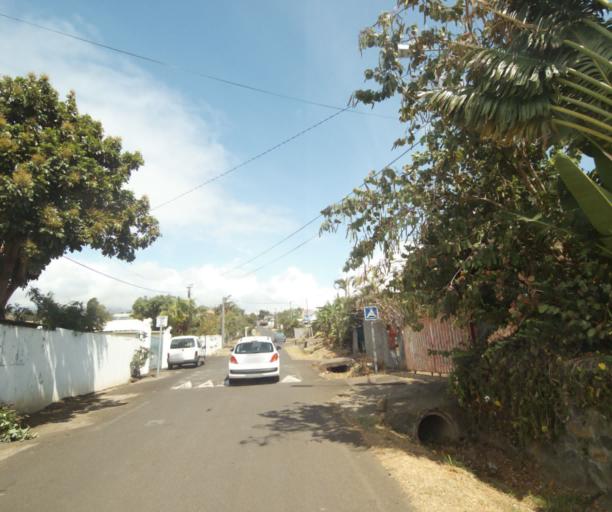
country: RE
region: Reunion
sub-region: Reunion
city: Saint-Paul
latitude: -21.0556
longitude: 55.2604
